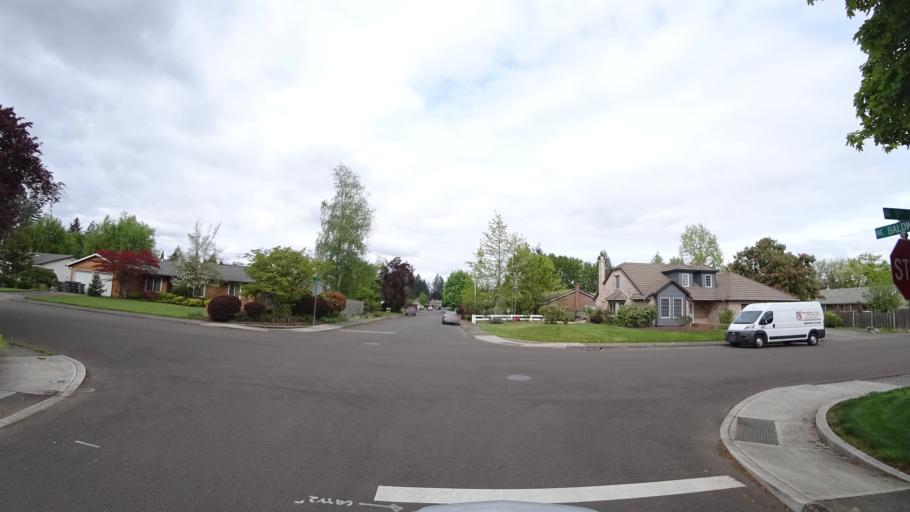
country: US
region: Oregon
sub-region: Washington County
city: Hillsboro
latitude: 45.5343
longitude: -122.9755
